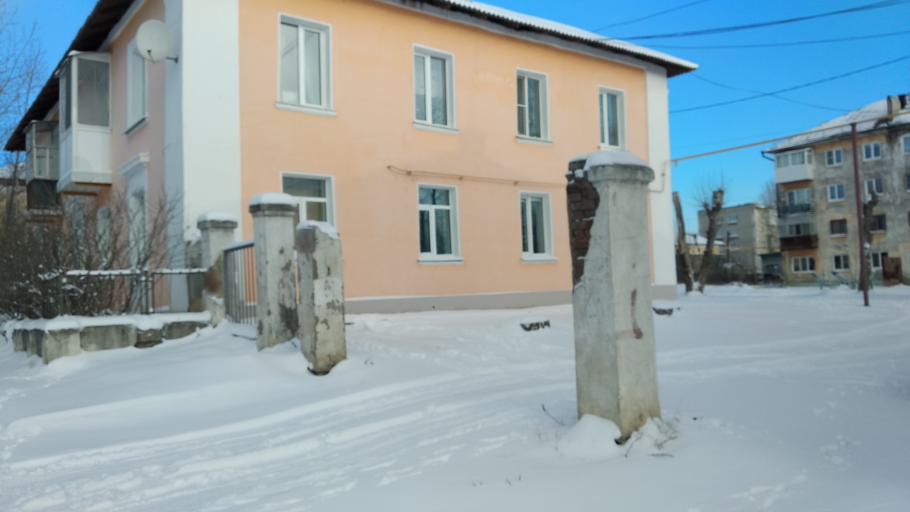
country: RU
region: Sverdlovsk
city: Krasnotur'insk
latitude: 59.7657
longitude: 60.1806
